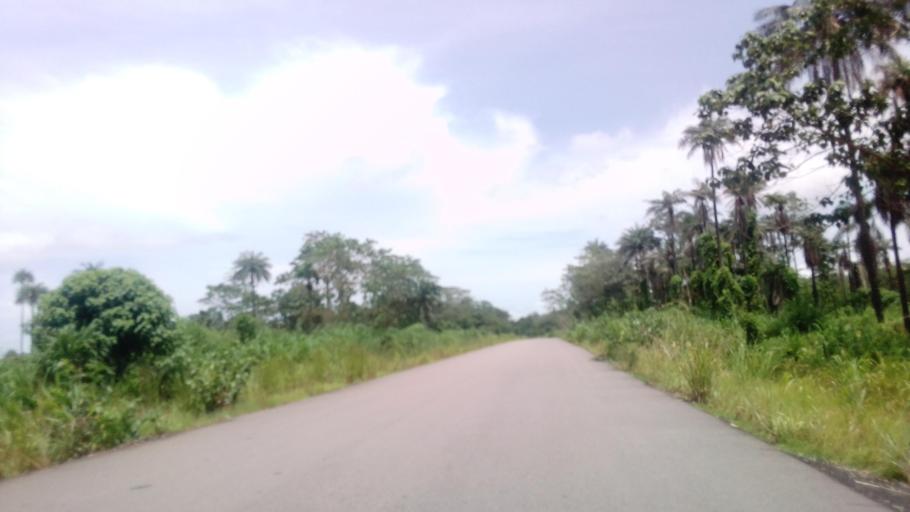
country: SL
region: Northern Province
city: Makeni
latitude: 9.0486
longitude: -12.1727
